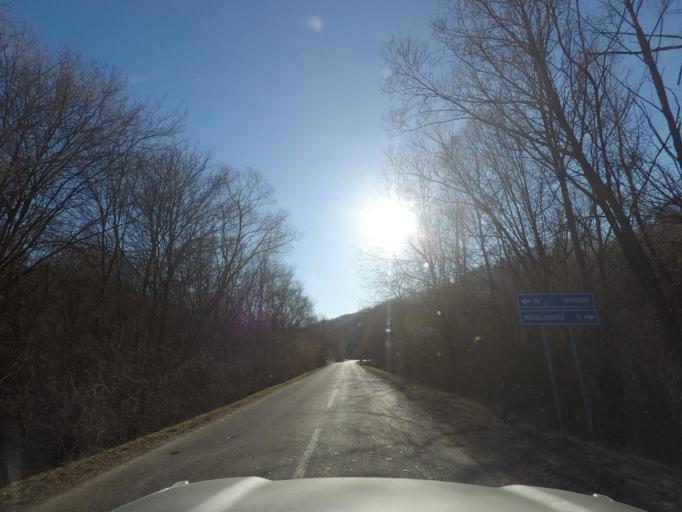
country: SK
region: Presovsky
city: Medzilaborce
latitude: 49.1656
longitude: 22.0216
